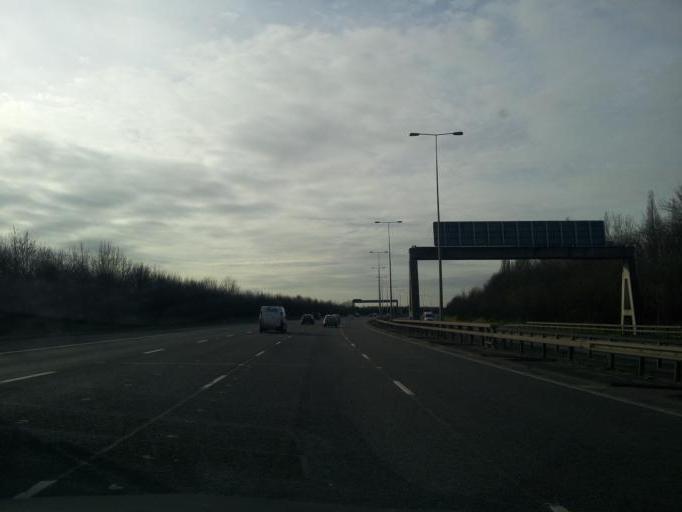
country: GB
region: England
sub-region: Cambridgeshire
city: Stilton
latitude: 52.4904
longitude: -0.2850
